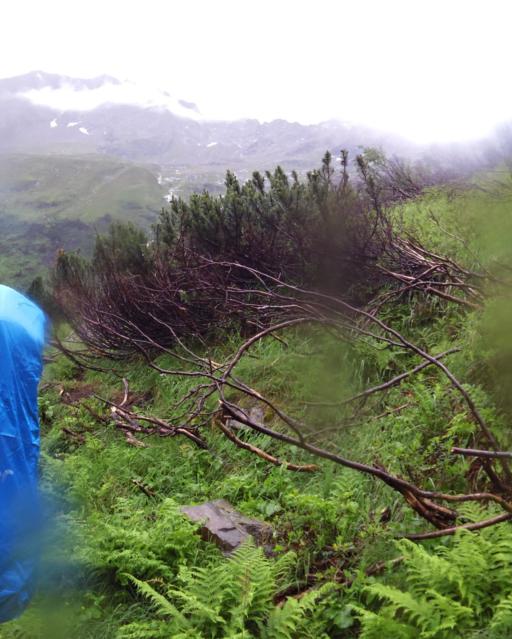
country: AT
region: Tyrol
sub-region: Politischer Bezirk Innsbruck Land
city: Neustift im Stubaital
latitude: 47.0088
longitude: 11.2220
